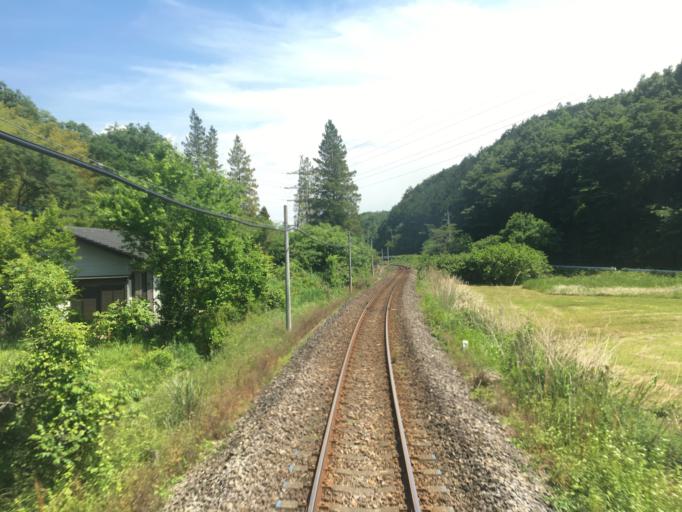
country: JP
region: Saitama
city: Yorii
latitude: 36.0840
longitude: 139.2151
